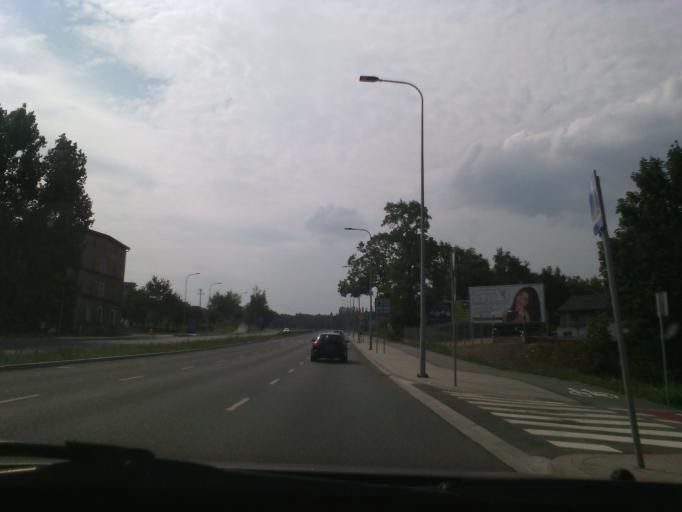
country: PL
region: Lower Silesian Voivodeship
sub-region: Powiat walbrzyski
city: Walbrzych
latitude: 50.7691
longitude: 16.2733
